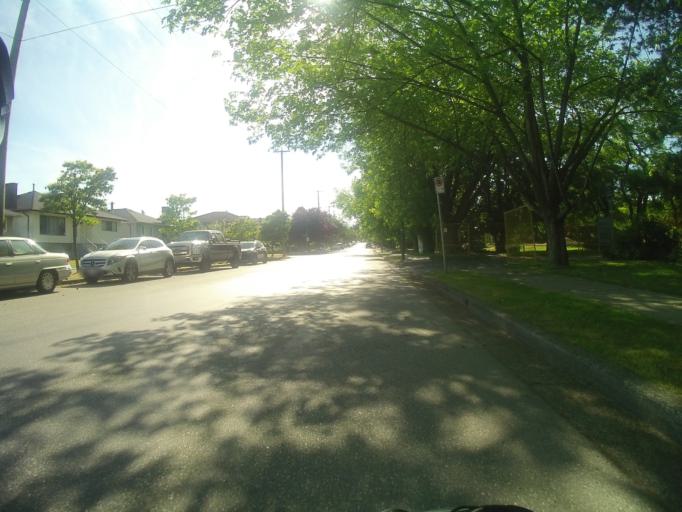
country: CA
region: British Columbia
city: Vancouver
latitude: 49.2170
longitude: -123.1192
